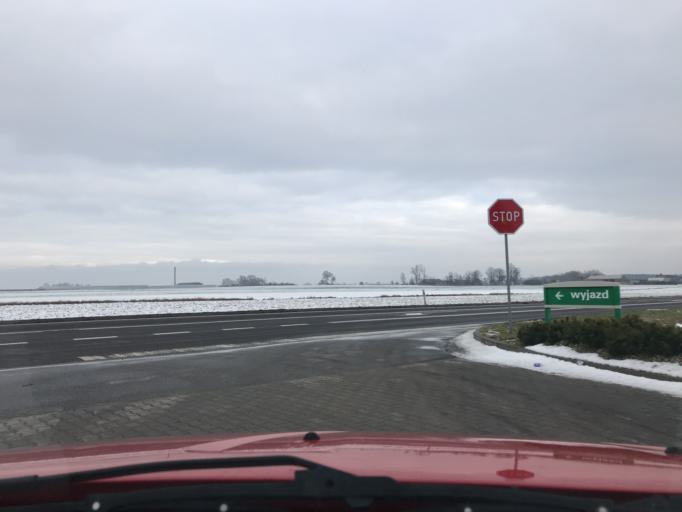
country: PL
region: Greater Poland Voivodeship
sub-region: Powiat pleszewski
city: Pleszew
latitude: 51.8888
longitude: 17.8452
